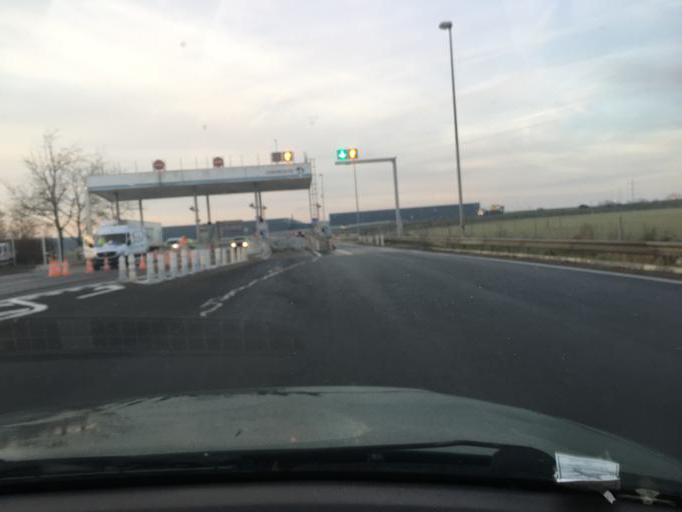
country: FR
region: Centre
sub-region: Departement du Loiret
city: Baule
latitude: 47.8332
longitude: 1.6694
